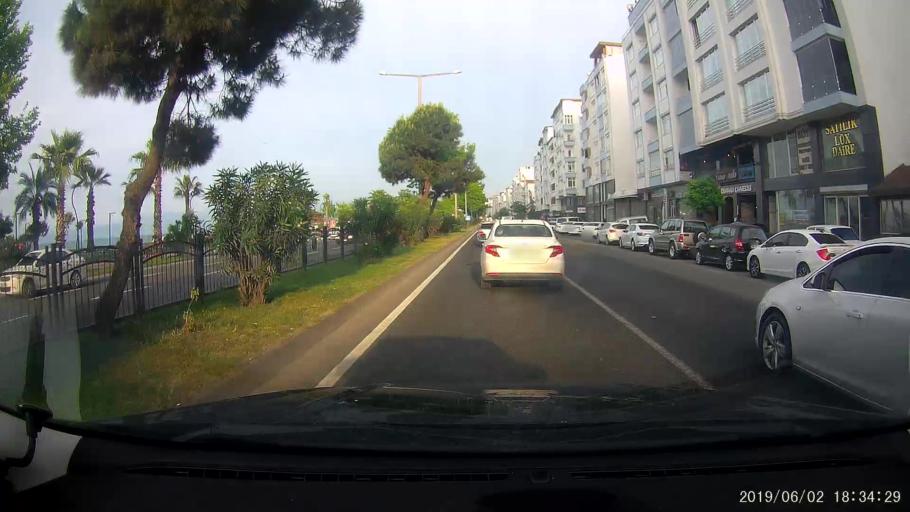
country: TR
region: Ordu
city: Fatsa
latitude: 41.0292
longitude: 37.5048
